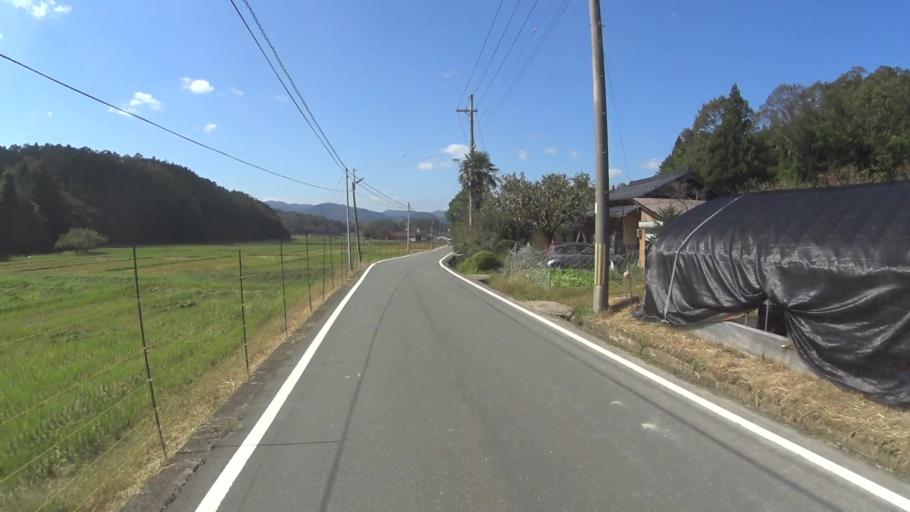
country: JP
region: Hyogo
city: Toyooka
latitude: 35.5946
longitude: 134.9690
